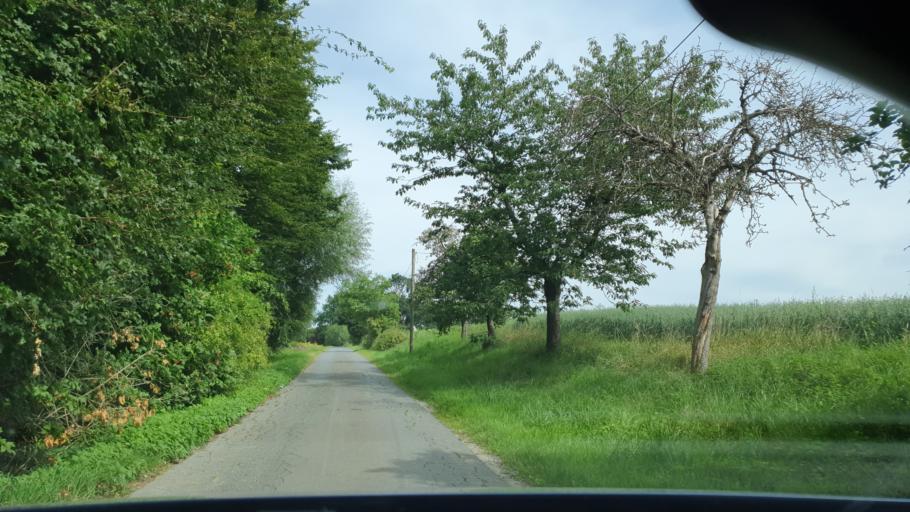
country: DE
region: North Rhine-Westphalia
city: Spenge
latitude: 52.1239
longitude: 8.4420
